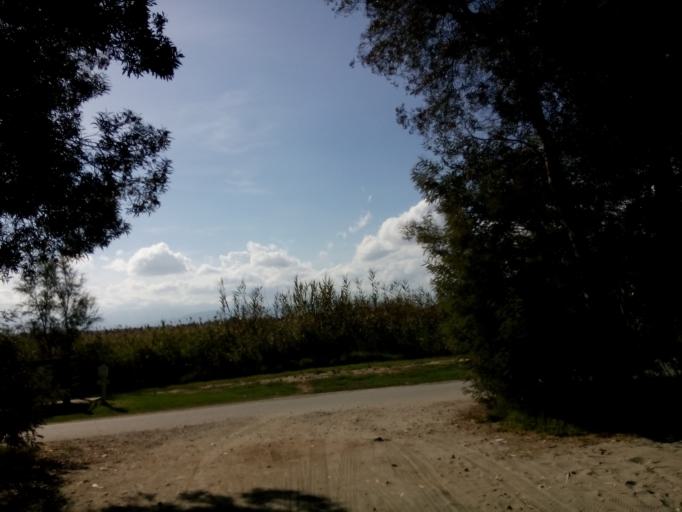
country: FR
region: Corsica
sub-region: Departement de la Haute-Corse
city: Aleria
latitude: 42.1083
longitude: 9.5488
